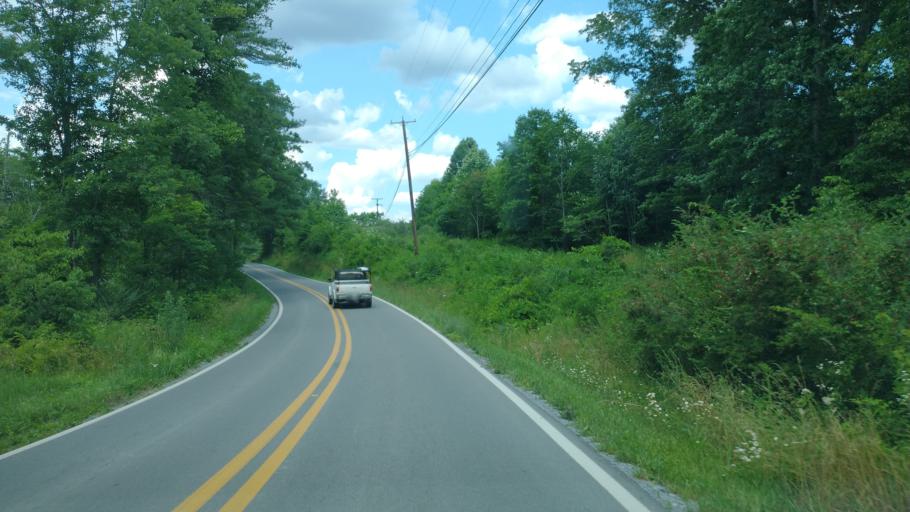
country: US
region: West Virginia
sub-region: Mercer County
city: Athens
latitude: 37.4314
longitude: -81.0623
